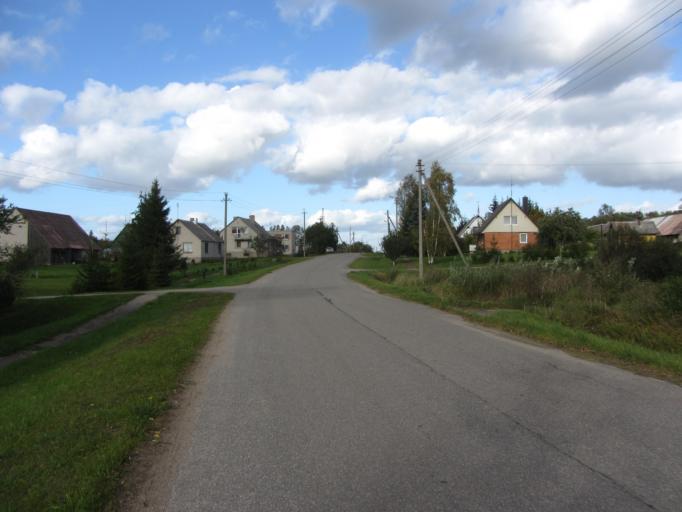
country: LT
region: Panevezys
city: Rokiskis
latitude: 55.9502
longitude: 25.7869
